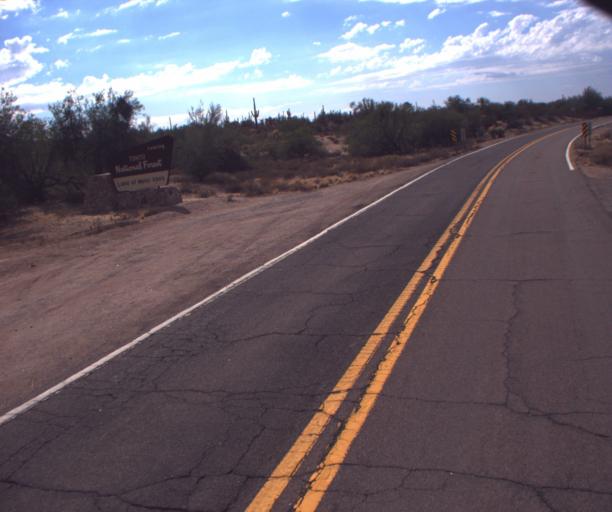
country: US
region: Arizona
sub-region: Pinal County
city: Apache Junction
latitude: 33.4666
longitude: -111.4796
